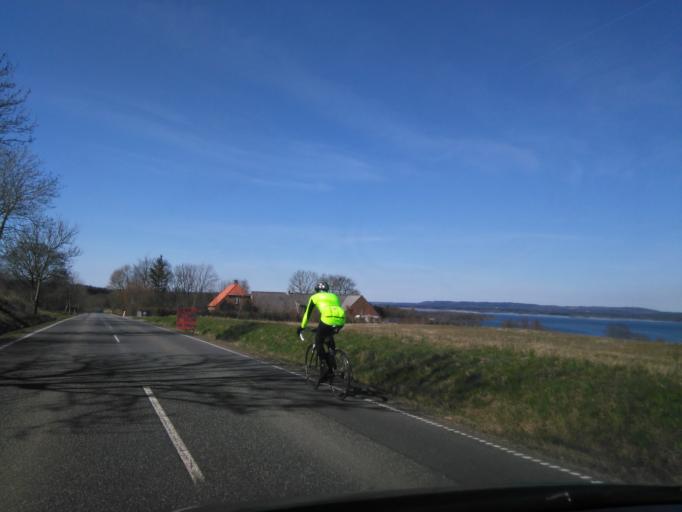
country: DK
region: Central Jutland
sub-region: Skanderborg Kommune
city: Ry
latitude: 56.0225
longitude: 9.8142
